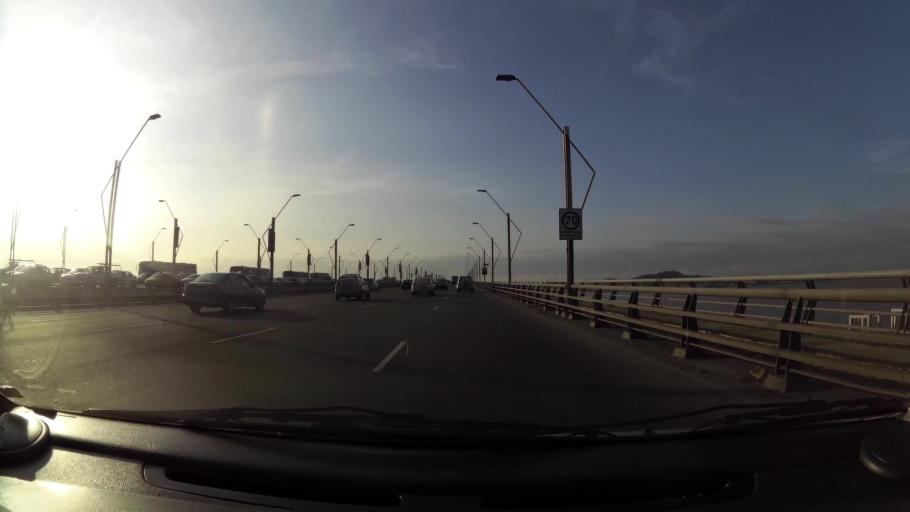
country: EC
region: Guayas
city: Eloy Alfaro
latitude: -2.1546
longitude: -79.8612
